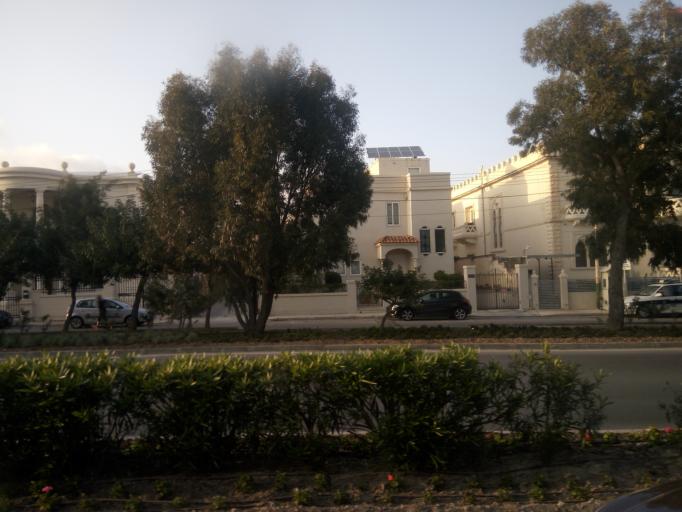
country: MT
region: Balzan
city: Balzan
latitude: 35.8933
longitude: 14.4539
